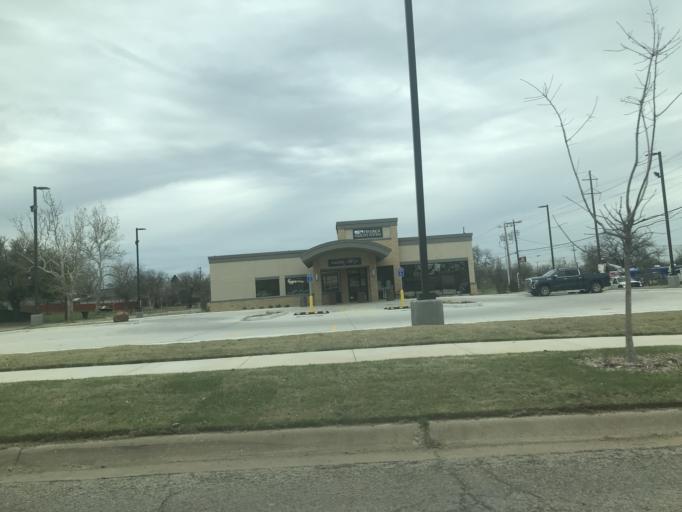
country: US
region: Texas
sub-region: Taylor County
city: Abilene
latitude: 32.4716
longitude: -99.7296
